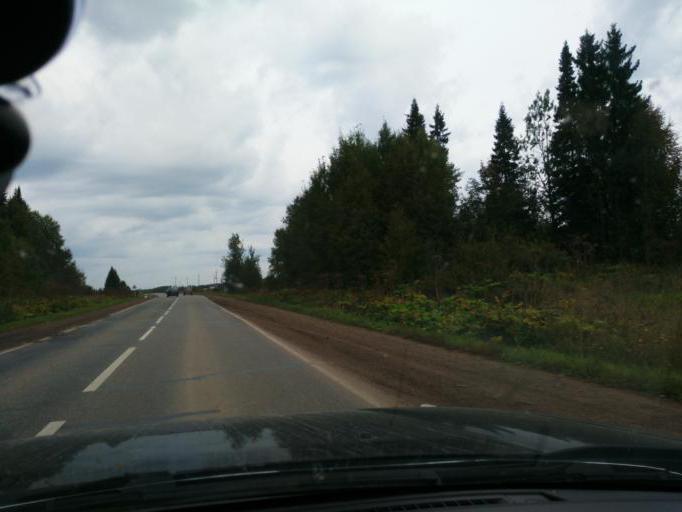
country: RU
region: Perm
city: Chernushka
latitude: 56.7349
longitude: 56.1730
